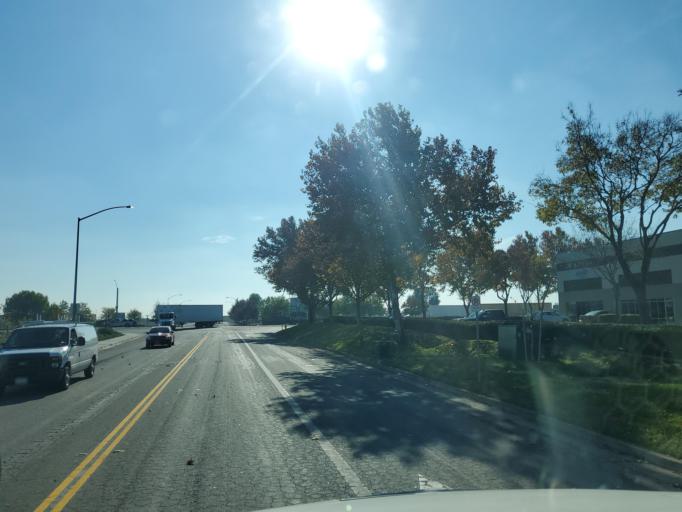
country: US
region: California
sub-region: San Joaquin County
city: Kennedy
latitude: 37.9078
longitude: -121.2388
